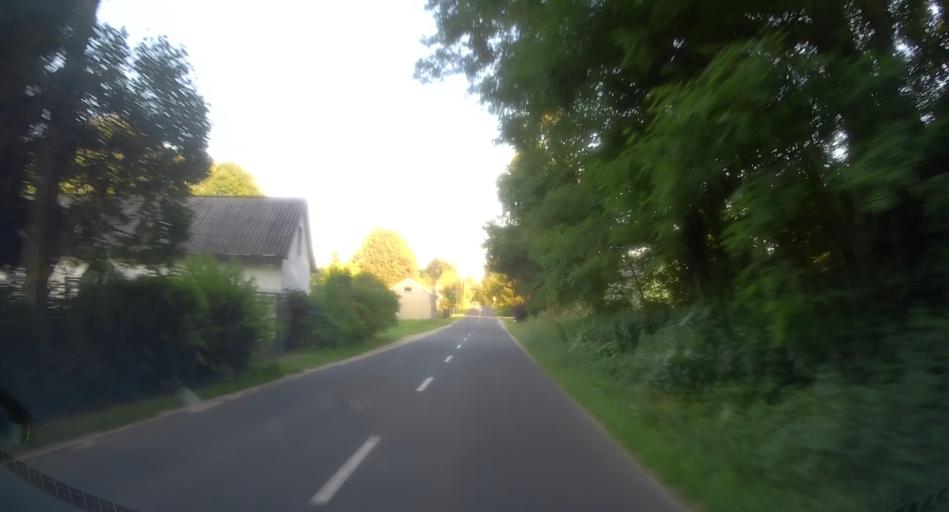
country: PL
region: Lodz Voivodeship
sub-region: Powiat skierniewicki
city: Kowiesy
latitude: 51.8992
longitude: 20.3726
